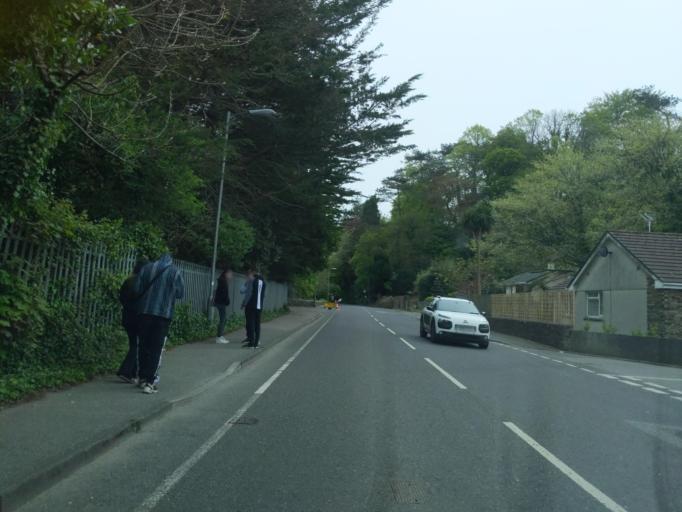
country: GB
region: England
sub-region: Cornwall
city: Par
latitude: 50.3548
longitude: -4.7114
